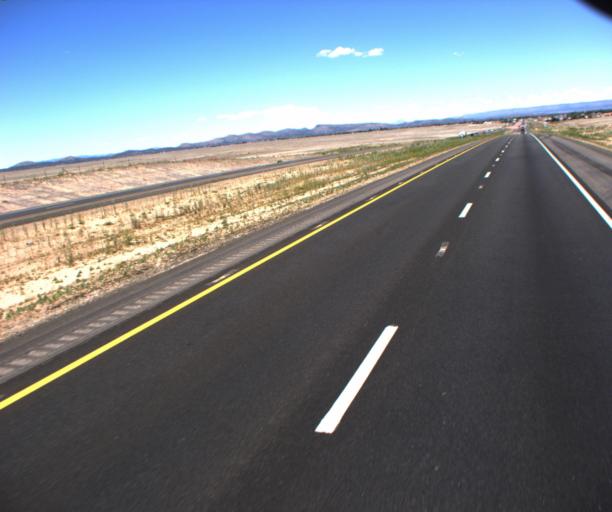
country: US
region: Arizona
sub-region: Yavapai County
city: Chino Valley
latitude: 34.6959
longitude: -112.4476
